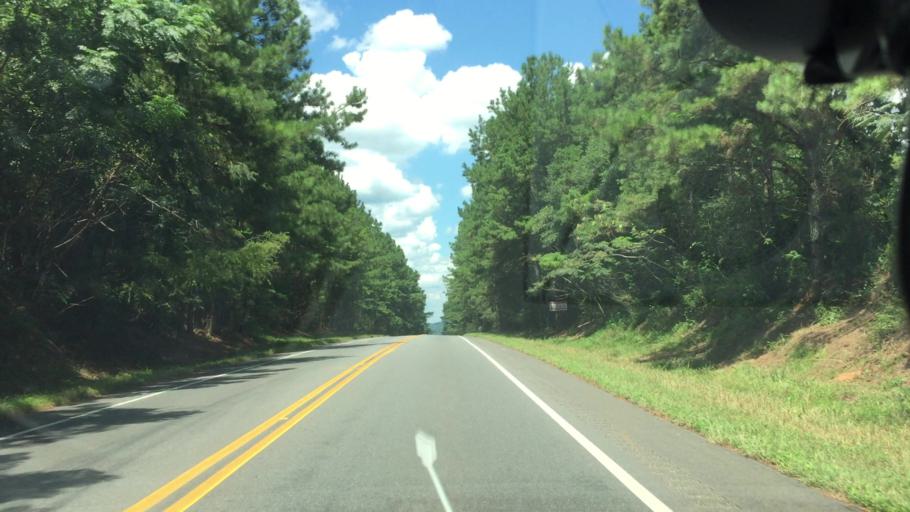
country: US
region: Alabama
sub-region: Coffee County
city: New Brockton
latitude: 31.4503
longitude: -85.8954
